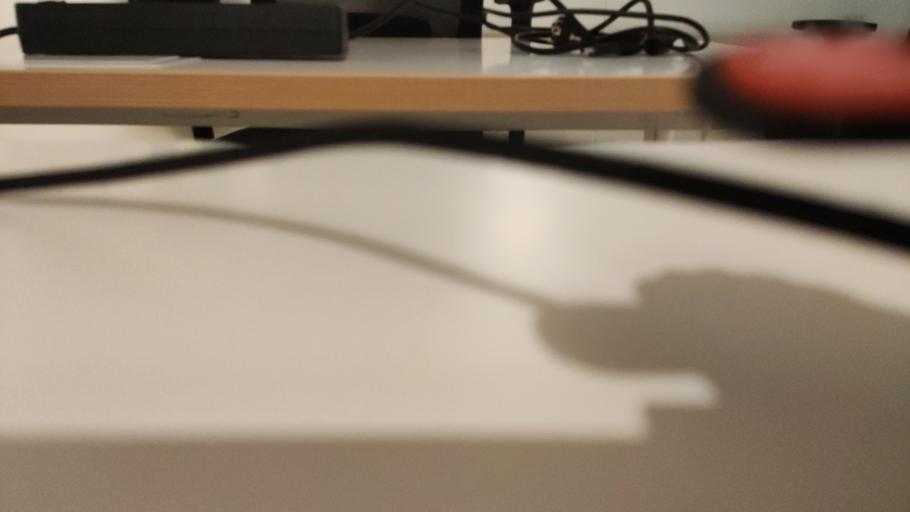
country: RU
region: Moskovskaya
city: Proletarskiy
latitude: 54.9757
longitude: 37.4071
